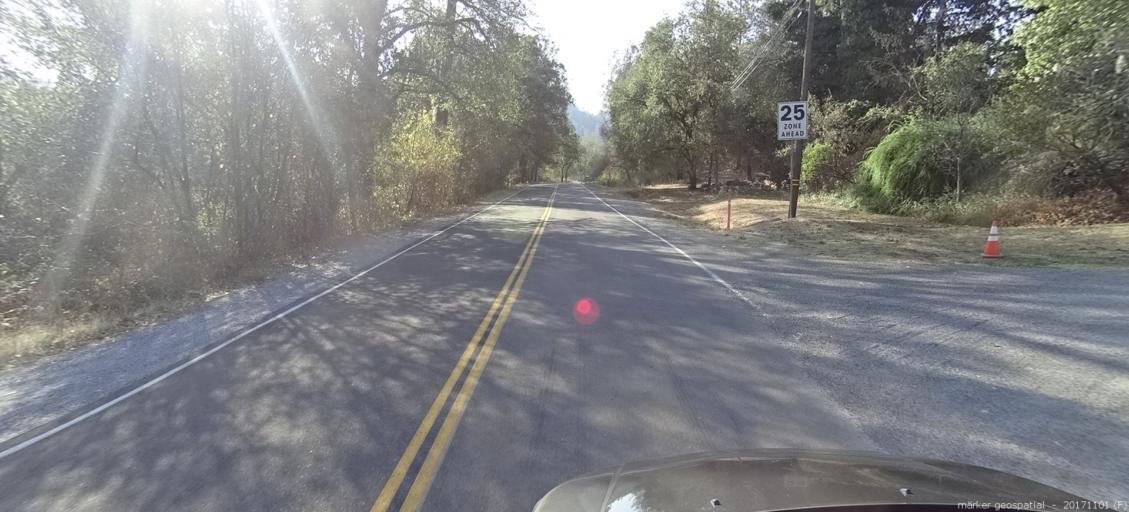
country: US
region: California
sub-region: Shasta County
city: Shasta Lake
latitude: 40.7301
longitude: -122.3243
